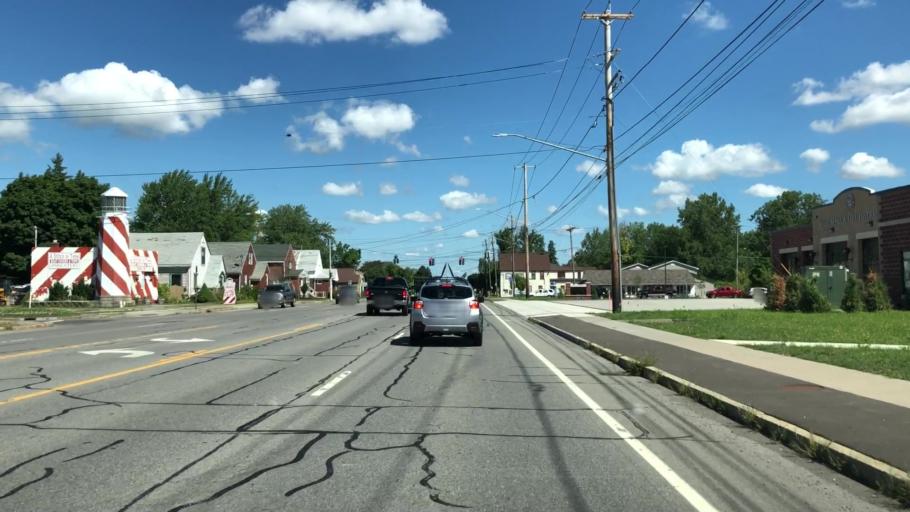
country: US
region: New York
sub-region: Erie County
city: West Seneca
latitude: 42.8501
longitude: -78.7544
